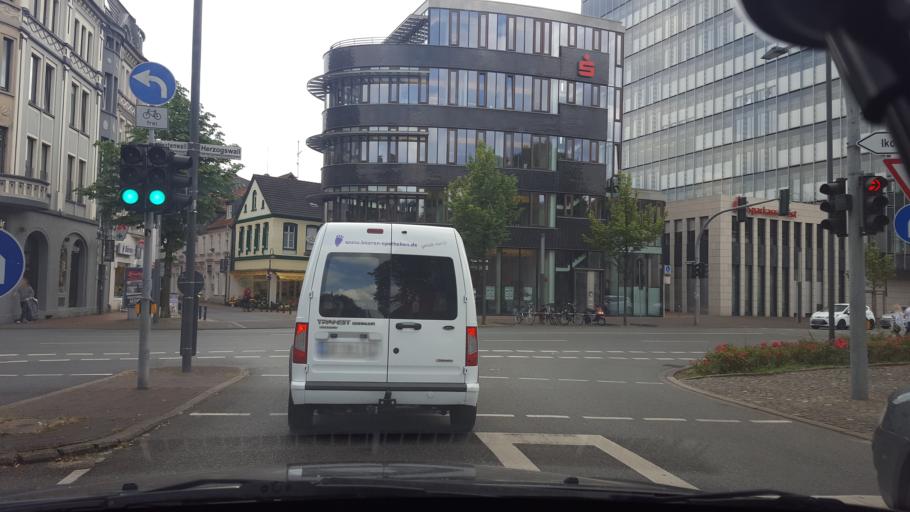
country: DE
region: North Rhine-Westphalia
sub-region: Regierungsbezirk Munster
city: Recklinghausen
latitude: 51.6169
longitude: 7.1980
